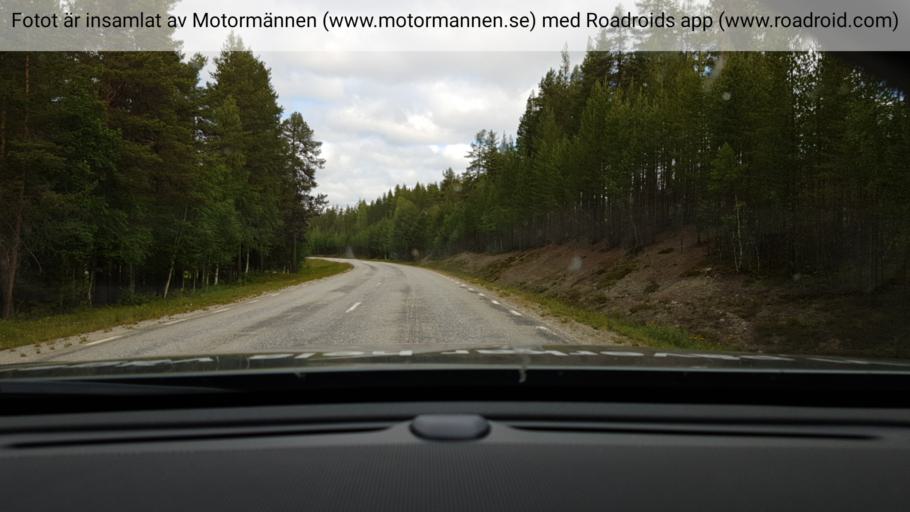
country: SE
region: Vaesterbotten
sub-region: Mala Kommun
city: Mala
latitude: 64.9424
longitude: 18.6238
